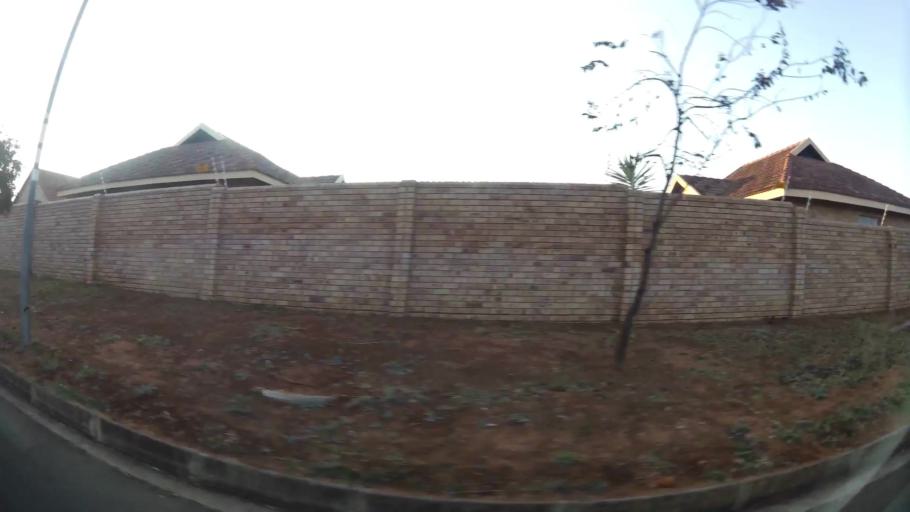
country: ZA
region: Orange Free State
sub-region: Mangaung Metropolitan Municipality
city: Bloemfontein
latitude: -29.1078
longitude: 26.1622
